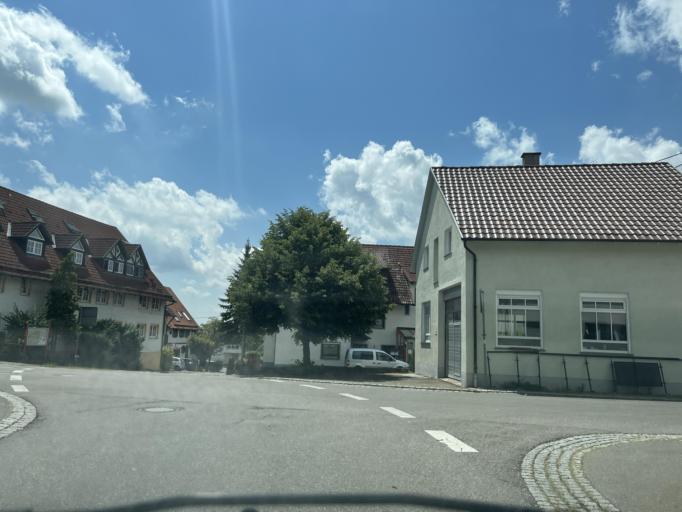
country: DE
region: Baden-Wuerttemberg
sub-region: Tuebingen Region
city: Leibertingen
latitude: 48.0071
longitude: 9.0383
